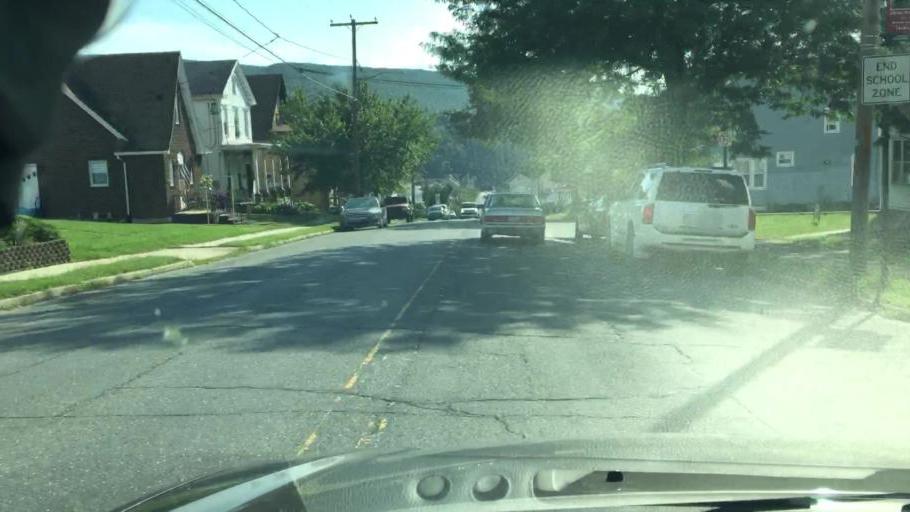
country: US
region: Pennsylvania
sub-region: Carbon County
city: Jim Thorpe
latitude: 40.8744
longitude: -75.7334
